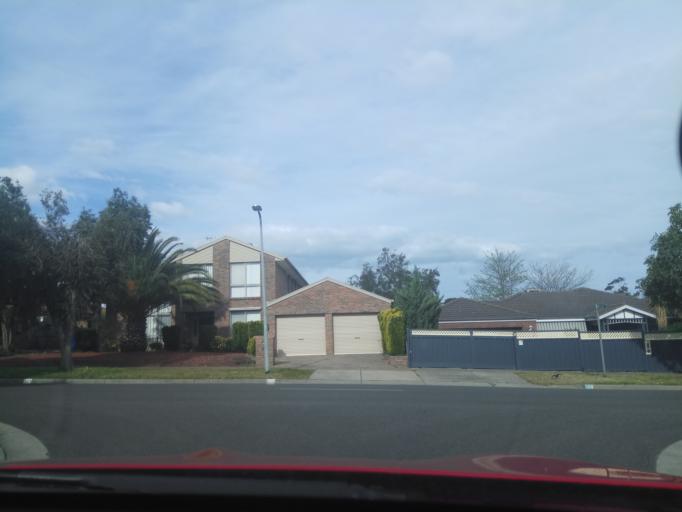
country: AU
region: Victoria
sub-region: Casey
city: Cranbourne North
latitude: -38.0730
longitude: 145.2757
